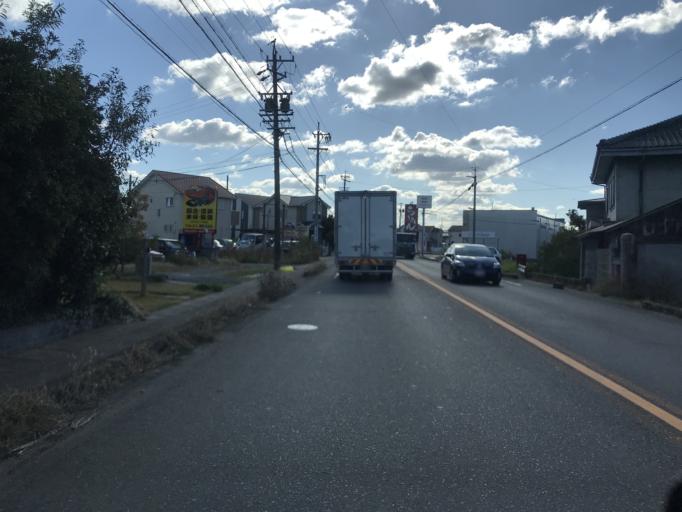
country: JP
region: Aichi
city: Inazawa
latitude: 35.2246
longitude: 136.8407
